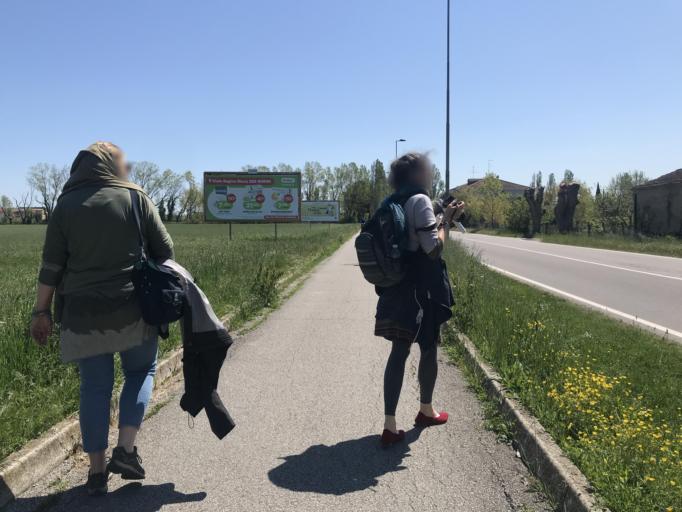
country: IT
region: Emilia-Romagna
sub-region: Provincia di Rimini
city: Rimini
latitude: 44.0744
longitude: 12.5495
